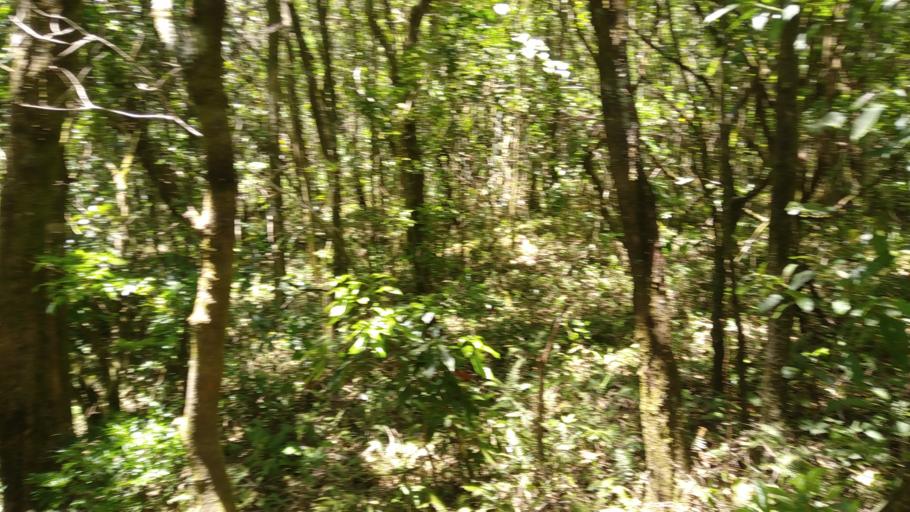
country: CR
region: Alajuela
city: Sabanilla
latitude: 10.1465
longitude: -84.2442
